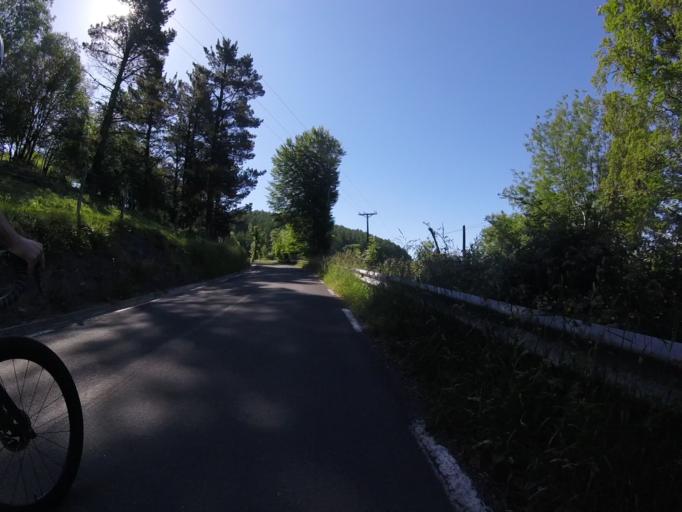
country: ES
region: Basque Country
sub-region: Provincia de Guipuzcoa
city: Beizama
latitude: 43.1233
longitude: -2.1859
